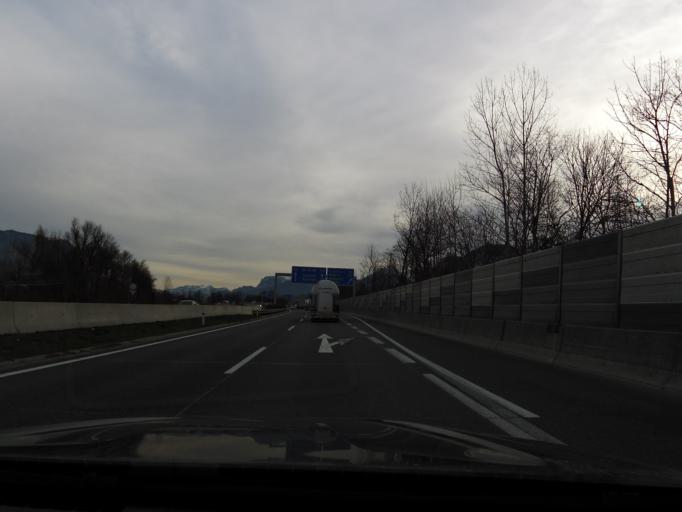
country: AT
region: Tyrol
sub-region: Politischer Bezirk Kufstein
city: Worgl
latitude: 47.4905
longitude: 12.0534
